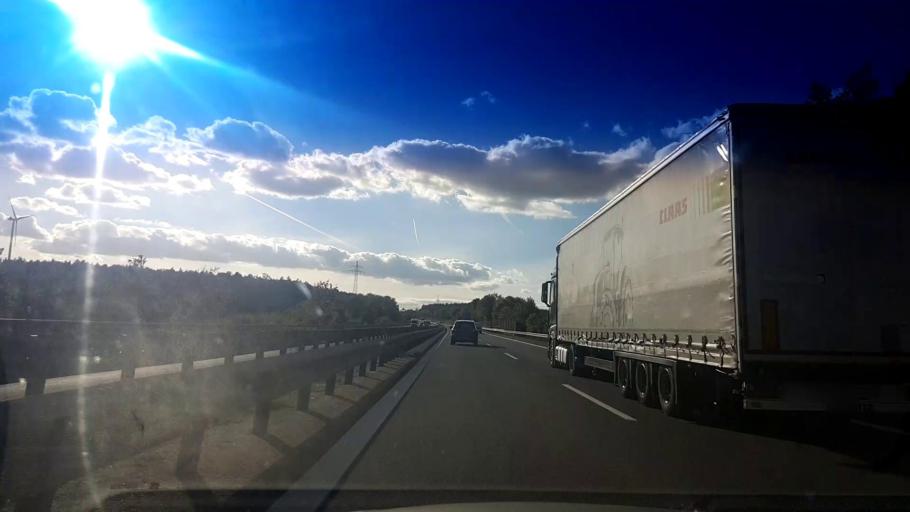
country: DE
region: Bavaria
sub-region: Upper Franconia
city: Wattendorf
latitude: 49.9875
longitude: 11.1391
